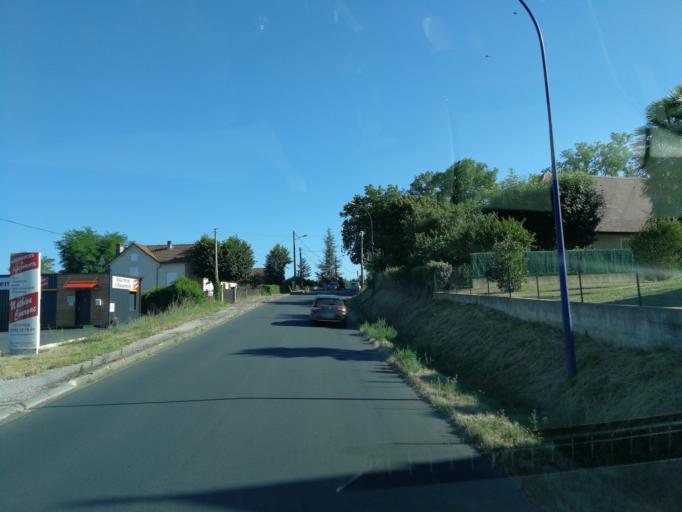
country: FR
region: Midi-Pyrenees
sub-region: Departement du Lot
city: Gourdon
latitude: 44.7303
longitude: 1.3739
